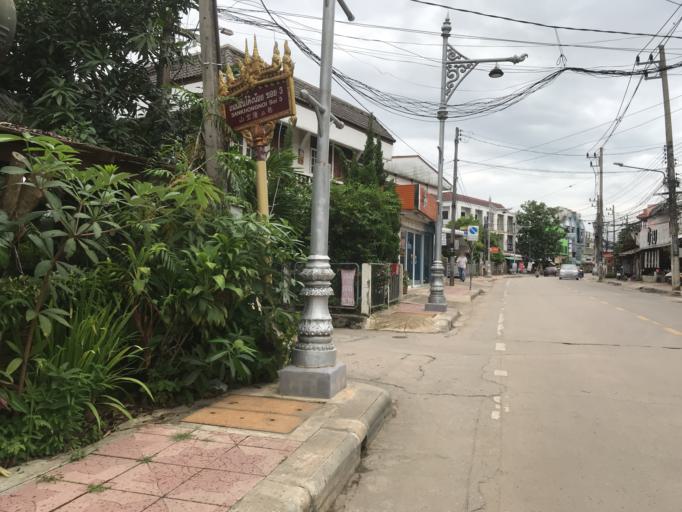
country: TH
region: Chiang Rai
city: Chiang Rai
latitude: 19.9018
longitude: 99.8248
